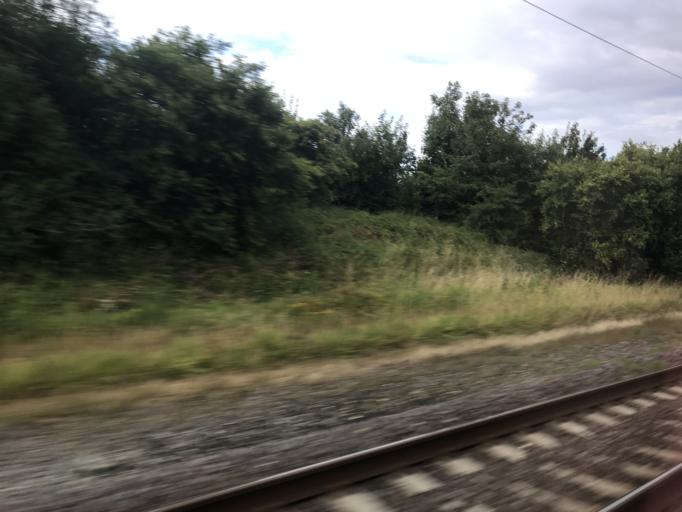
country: FR
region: Champagne-Ardenne
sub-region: Departement des Ardennes
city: Blagny
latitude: 49.6139
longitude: 5.2053
